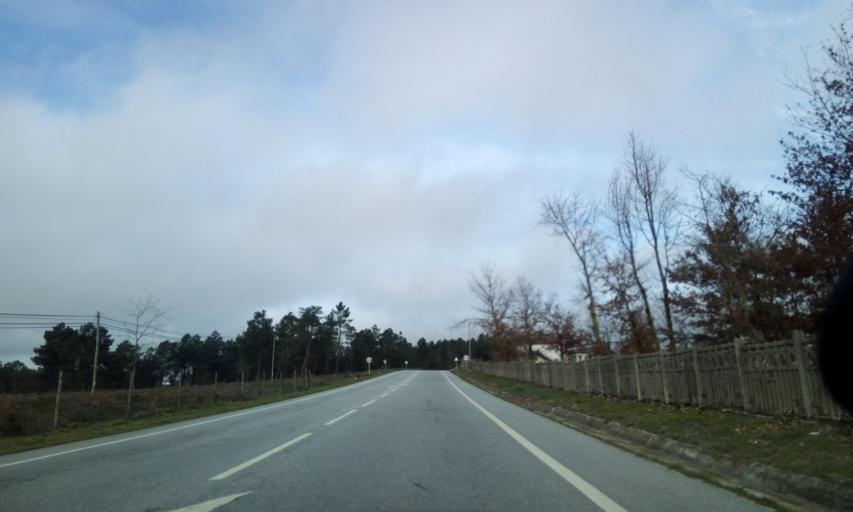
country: PT
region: Guarda
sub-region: Aguiar da Beira
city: Aguiar da Beira
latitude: 40.8077
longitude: -7.5295
